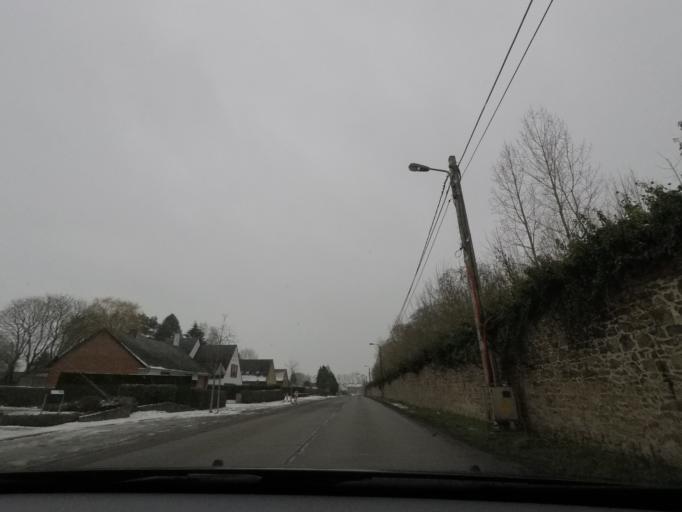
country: BE
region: Wallonia
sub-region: Province du Hainaut
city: Brugelette
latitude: 50.5888
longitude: 3.8506
